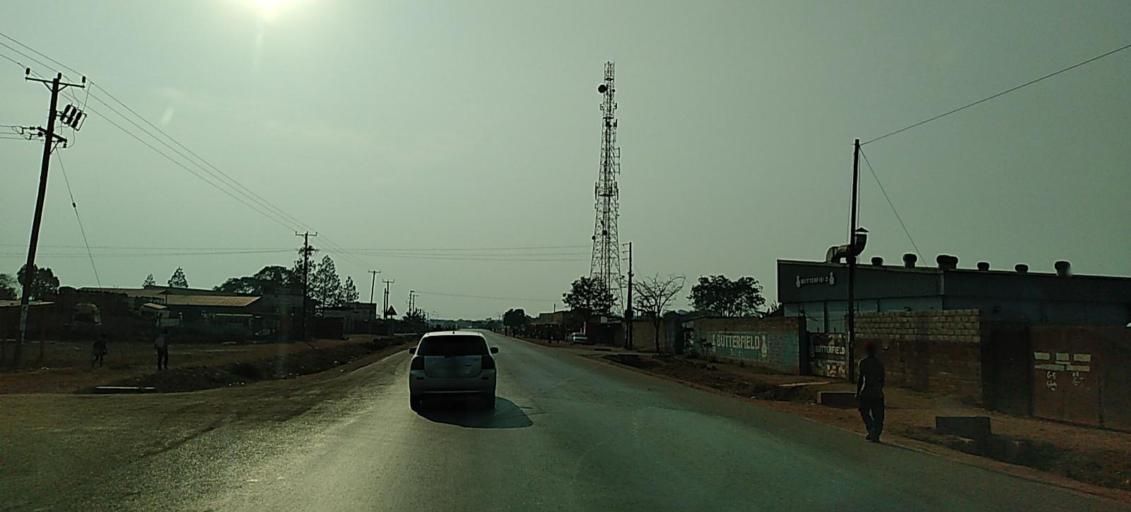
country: ZM
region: North-Western
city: Solwezi
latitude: -12.1922
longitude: 26.4436
